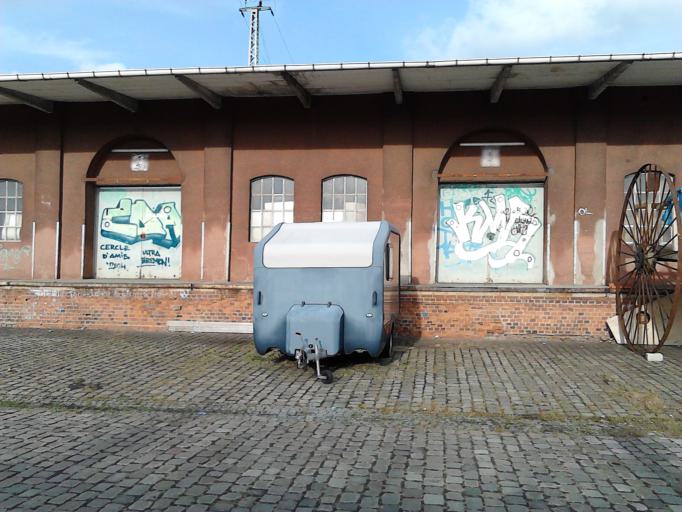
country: DE
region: Bremen
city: Bremen
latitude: 53.0859
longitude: 8.8065
